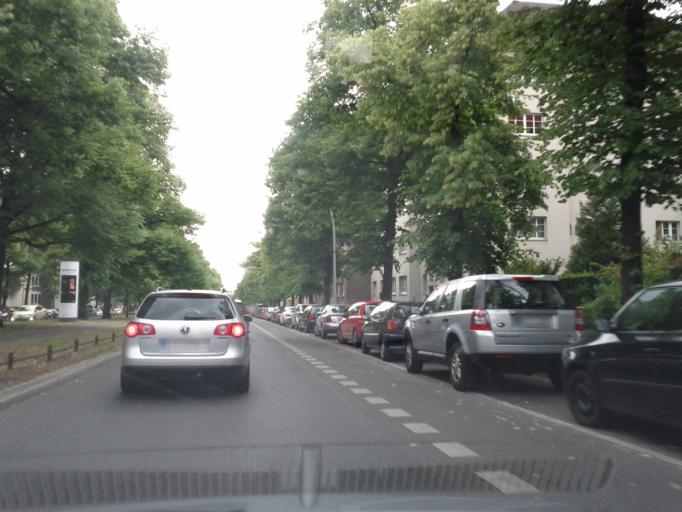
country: DE
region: Berlin
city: Westend
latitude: 52.5171
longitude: 13.2597
